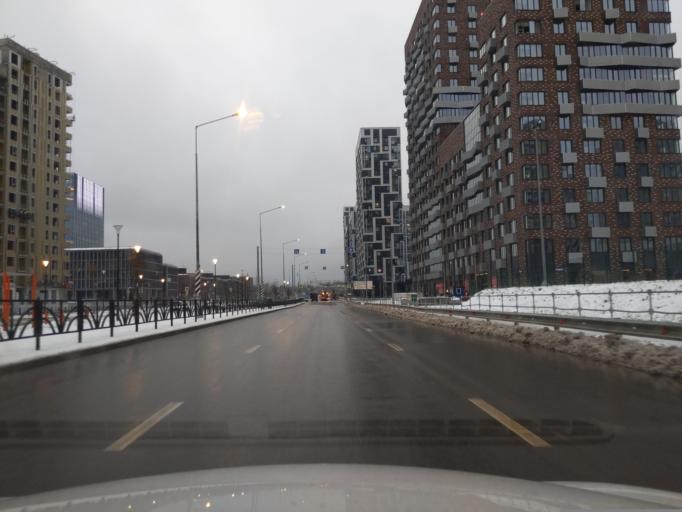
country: RU
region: Moscow
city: Strogino
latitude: 55.8180
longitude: 37.4267
